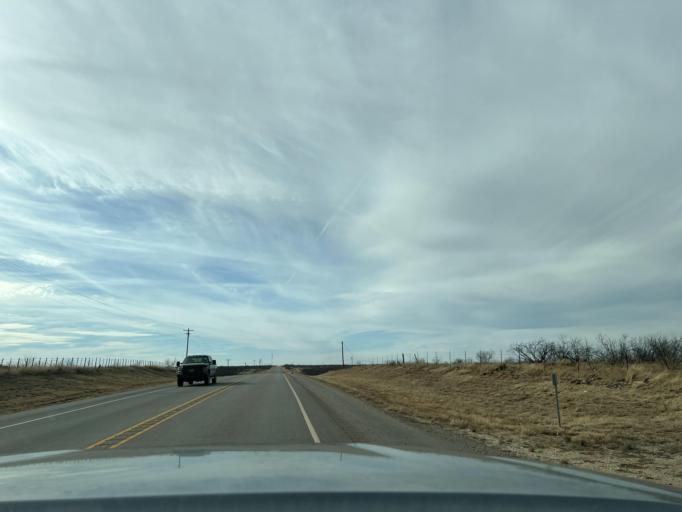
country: US
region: Texas
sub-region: Jones County
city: Anson
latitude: 32.7507
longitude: -99.6987
